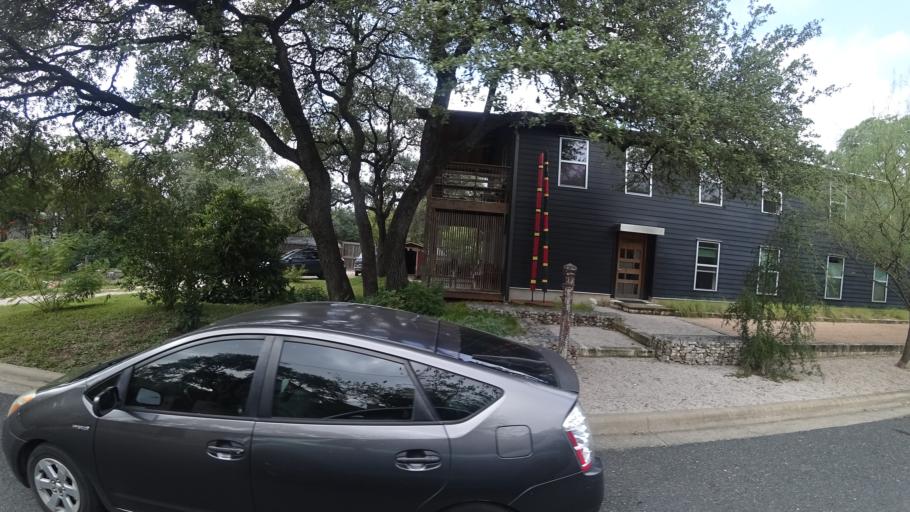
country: US
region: Texas
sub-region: Travis County
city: Austin
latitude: 30.2508
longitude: -97.7619
